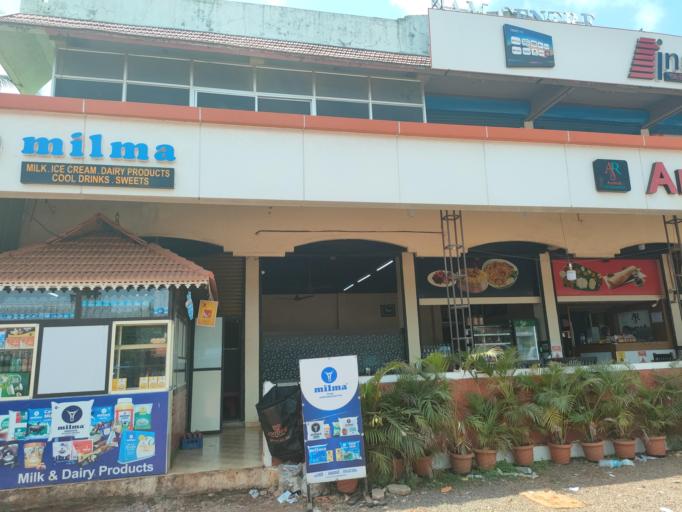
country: IN
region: Kerala
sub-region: Kasaragod District
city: Kasaragod
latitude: 12.5180
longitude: 75.0166
